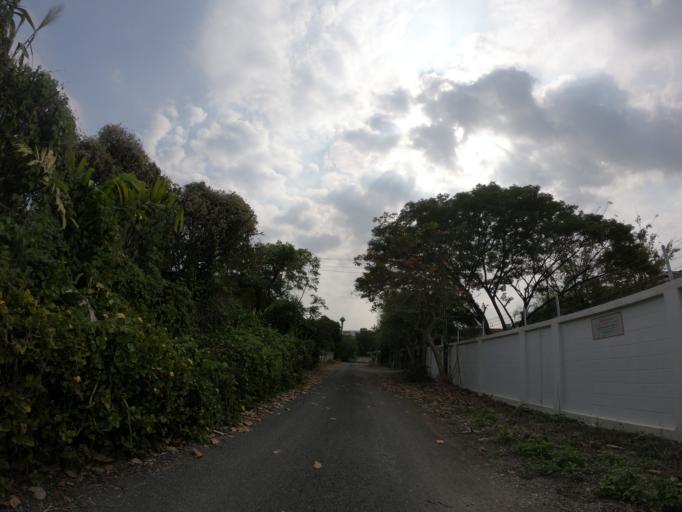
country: TH
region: Chiang Mai
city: Chiang Mai
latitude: 18.7584
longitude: 98.9668
